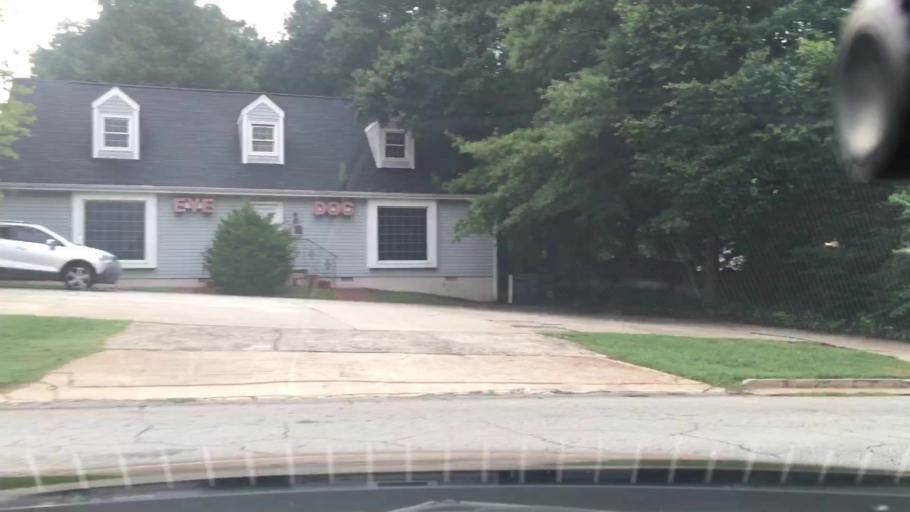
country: US
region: Georgia
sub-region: Spalding County
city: Griffin
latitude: 33.2467
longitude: -84.2781
